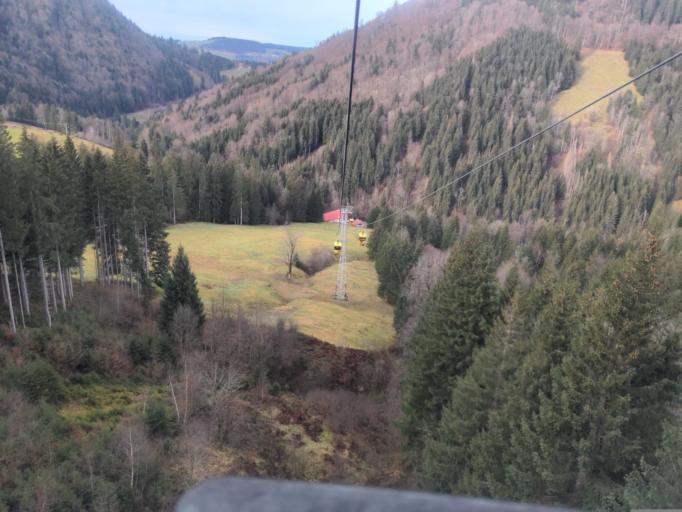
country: DE
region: Bavaria
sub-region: Swabia
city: Balderschwang
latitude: 47.5060
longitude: 10.0611
